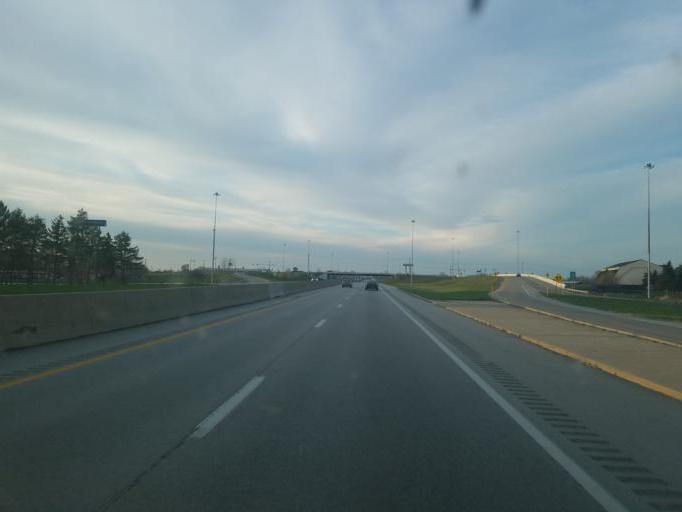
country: US
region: Ohio
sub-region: Wood County
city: Northwood
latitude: 41.6123
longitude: -83.4769
